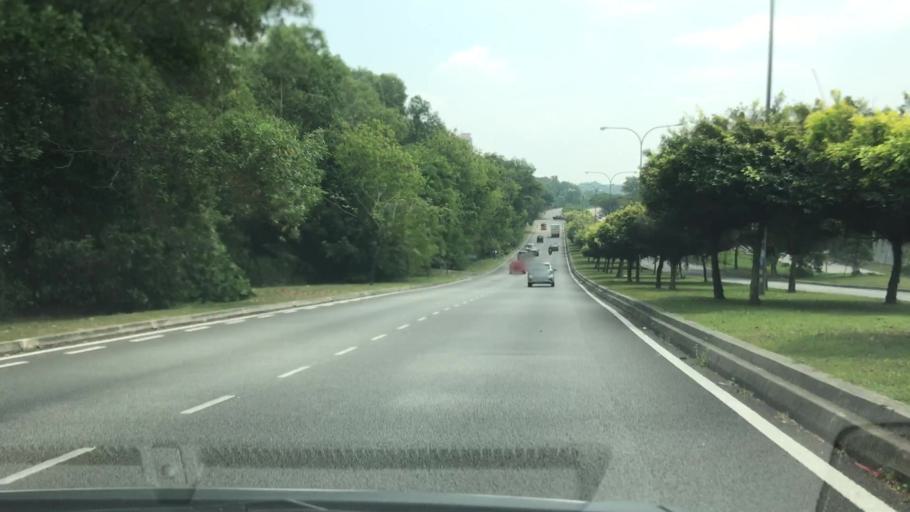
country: MY
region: Putrajaya
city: Putrajaya
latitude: 3.0021
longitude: 101.6650
